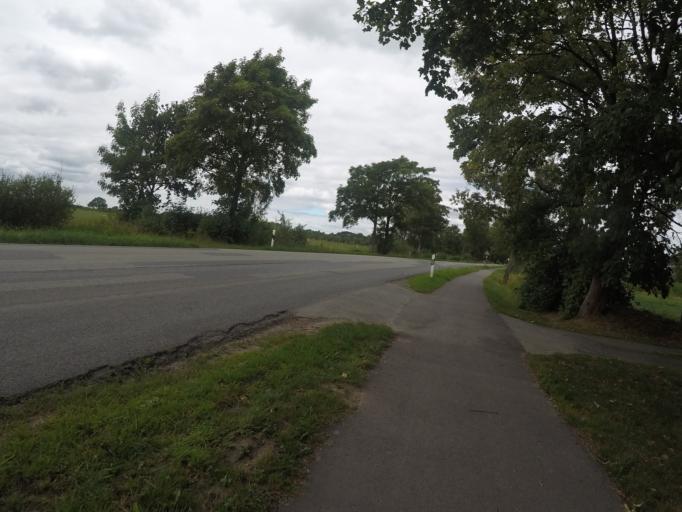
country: DE
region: Lower Saxony
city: Himmelpforten
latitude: 53.6480
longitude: 9.2970
